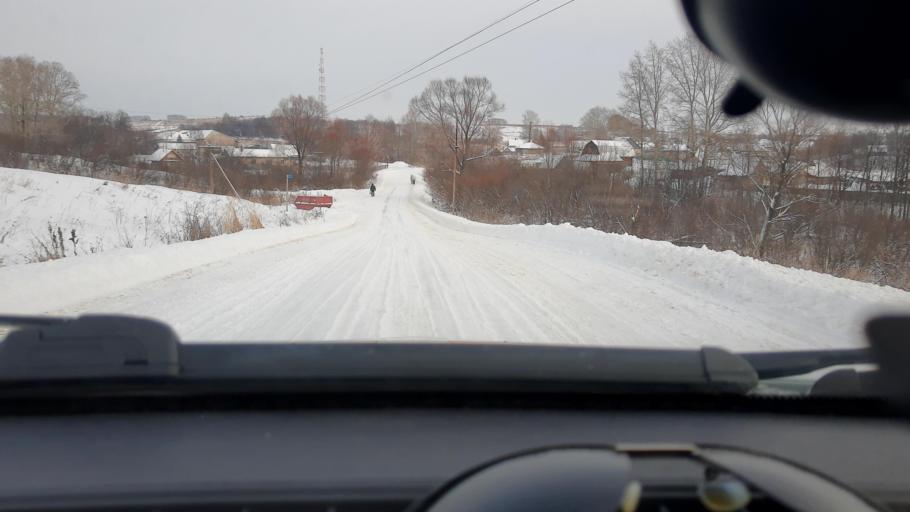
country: RU
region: Bashkortostan
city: Yazykovo
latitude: 55.0331
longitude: 56.2304
